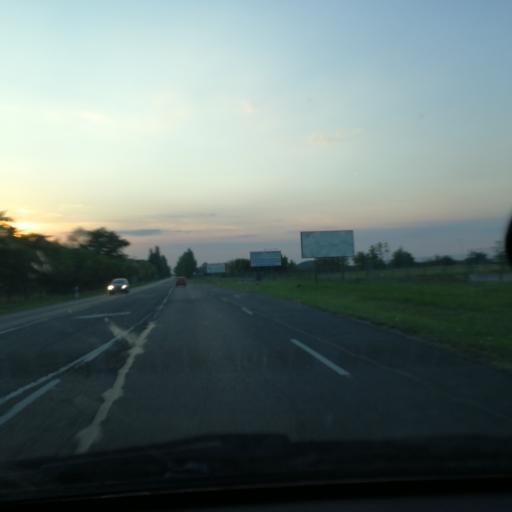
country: HU
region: Bacs-Kiskun
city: Kiskoros
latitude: 46.6042
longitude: 19.3137
